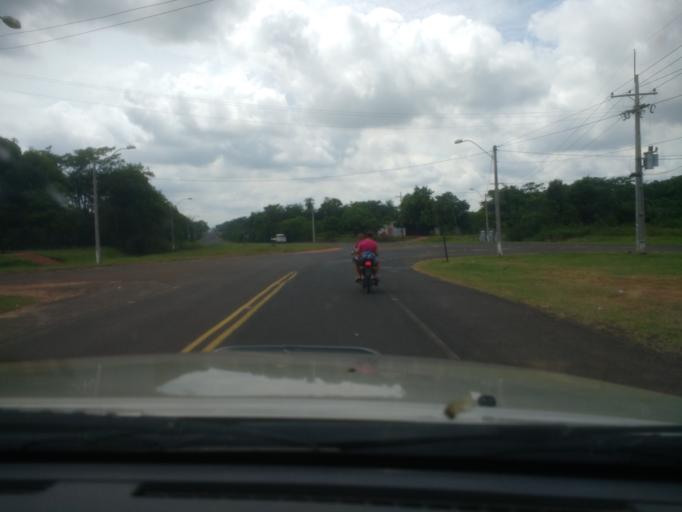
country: PY
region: San Pedro
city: Puerto Rosario
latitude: -24.4242
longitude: -57.0860
